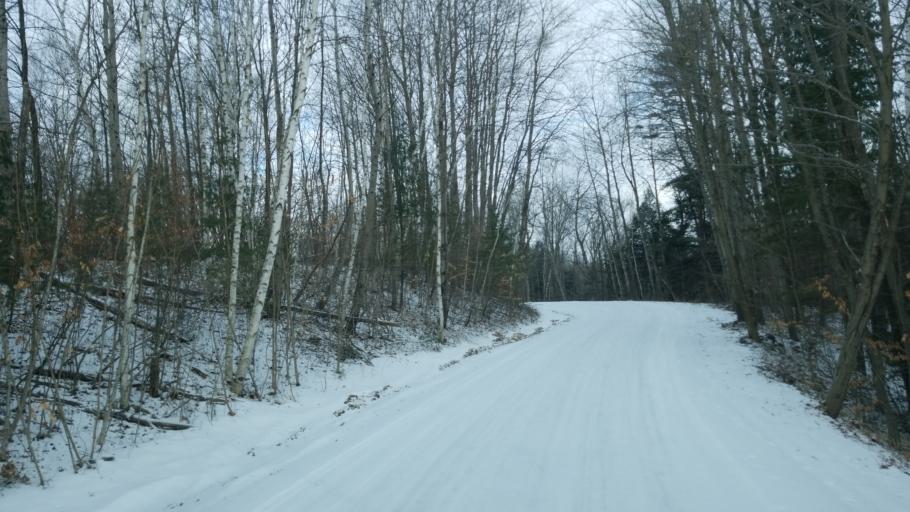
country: US
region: Michigan
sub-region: Osceola County
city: Evart
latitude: 43.8122
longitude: -85.2677
